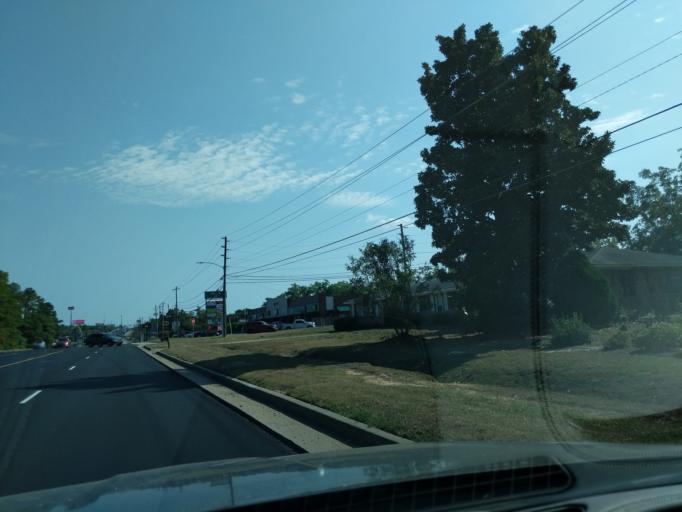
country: US
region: Georgia
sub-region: Columbia County
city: Evans
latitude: 33.4904
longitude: -82.1363
